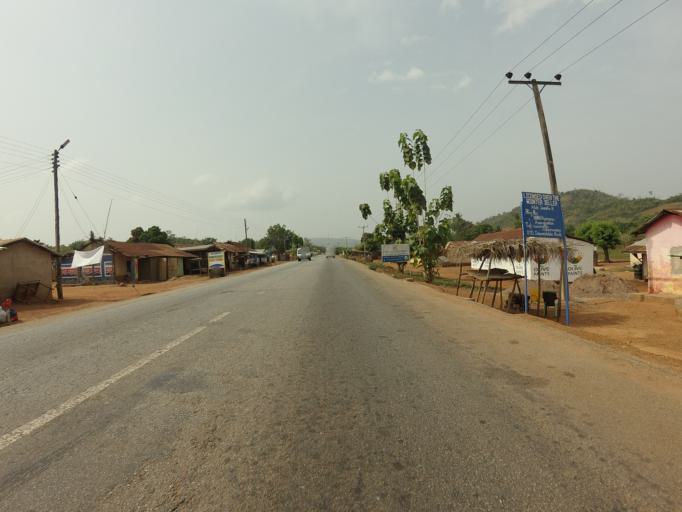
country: GH
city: Akropong
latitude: 6.3146
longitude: 0.1568
